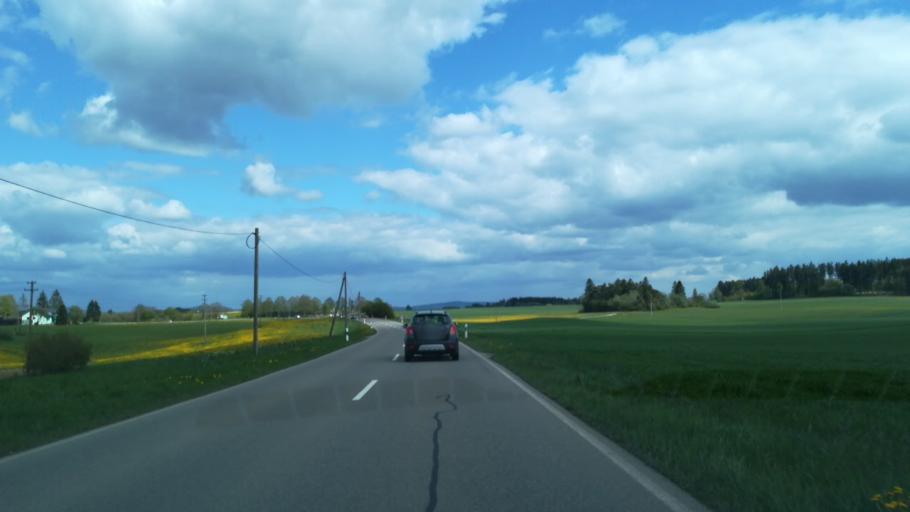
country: DE
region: Baden-Wuerttemberg
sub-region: Freiburg Region
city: Bonndorf im Schwarzwald
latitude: 47.8207
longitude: 8.3652
